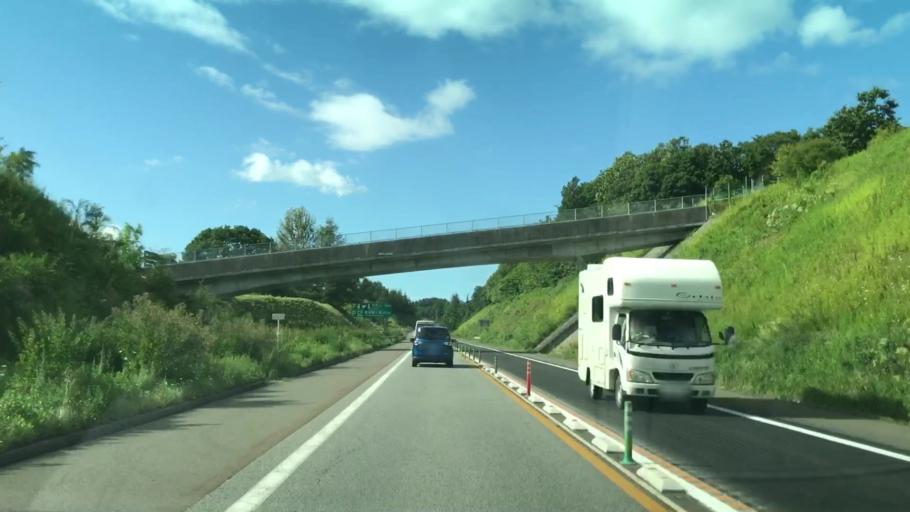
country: JP
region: Hokkaido
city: Date
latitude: 42.4386
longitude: 140.9195
